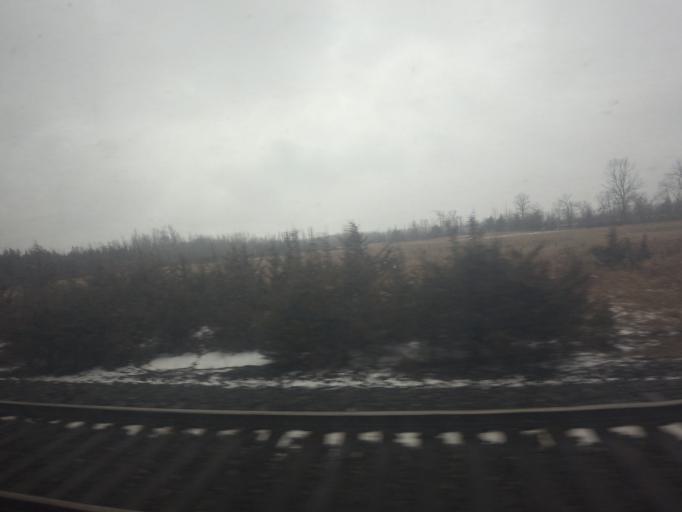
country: CA
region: Ontario
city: Belleville
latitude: 44.2042
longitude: -77.2657
